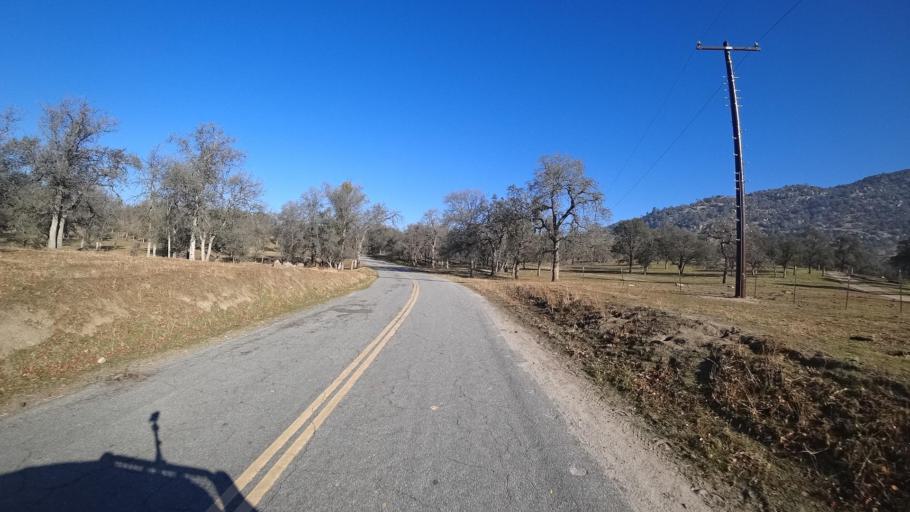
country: US
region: California
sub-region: Kern County
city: Alta Sierra
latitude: 35.7545
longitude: -118.8182
